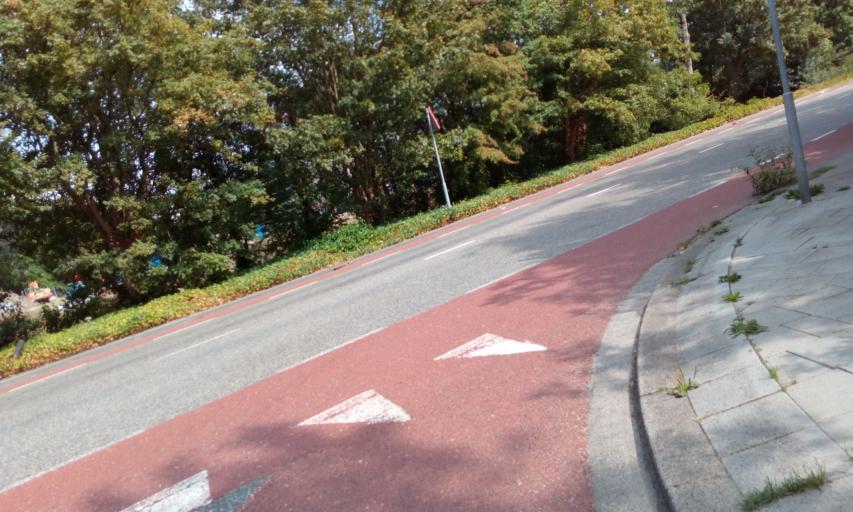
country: NL
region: South Holland
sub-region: Gemeente Vlaardingen
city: Vlaardingen
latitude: 51.9311
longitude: 4.3594
